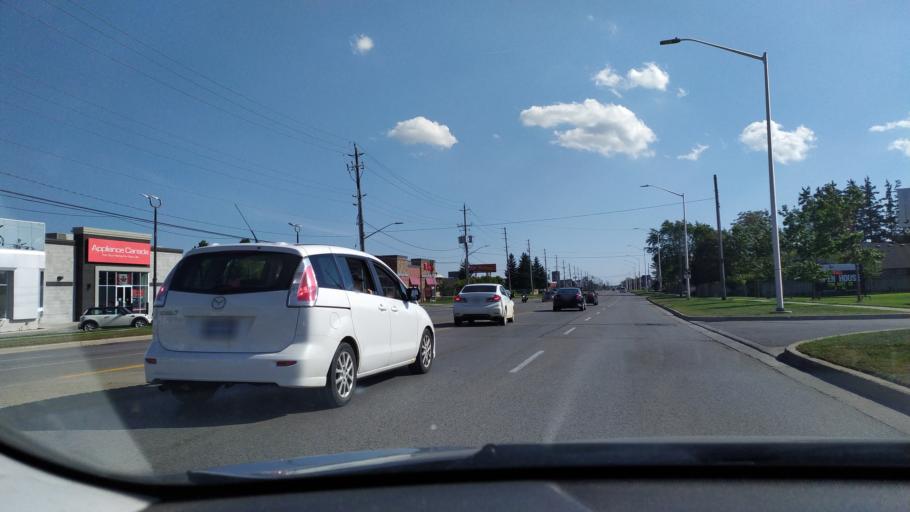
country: CA
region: Ontario
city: London
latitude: 42.9533
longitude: -81.2598
